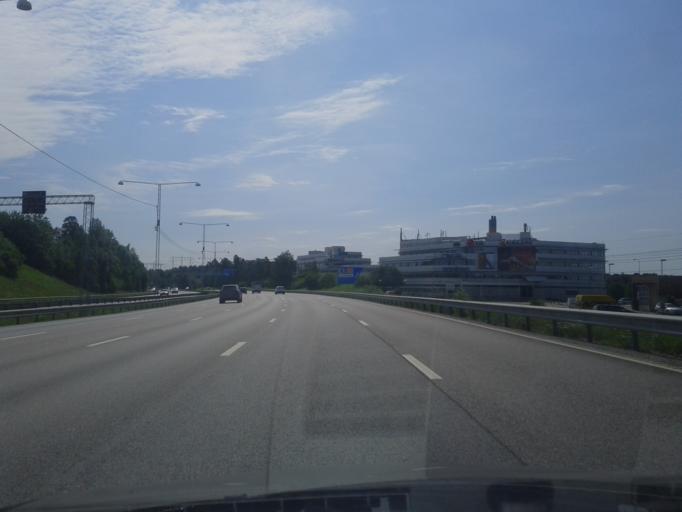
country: SE
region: Stockholm
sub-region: Sollentuna Kommun
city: Sollentuna
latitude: 59.4219
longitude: 17.9250
